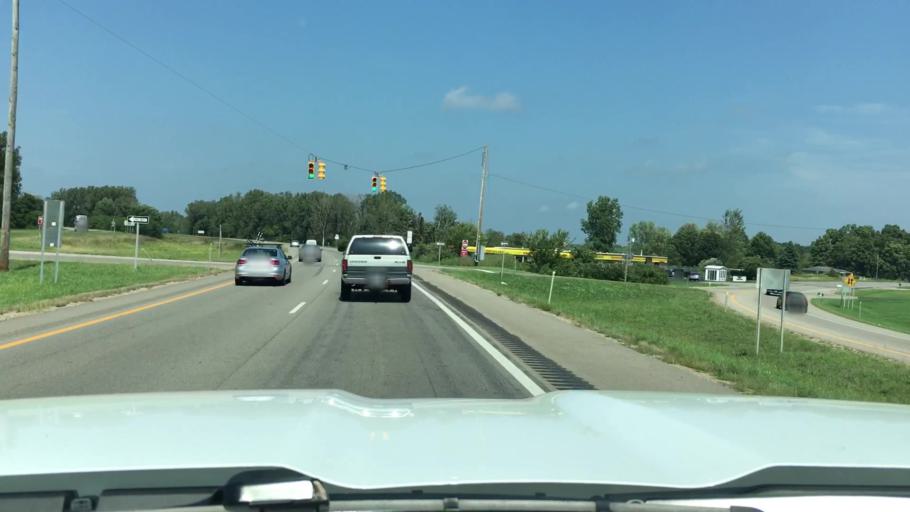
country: US
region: Michigan
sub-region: Kalamazoo County
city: Schoolcraft
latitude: 42.1454
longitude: -85.6377
